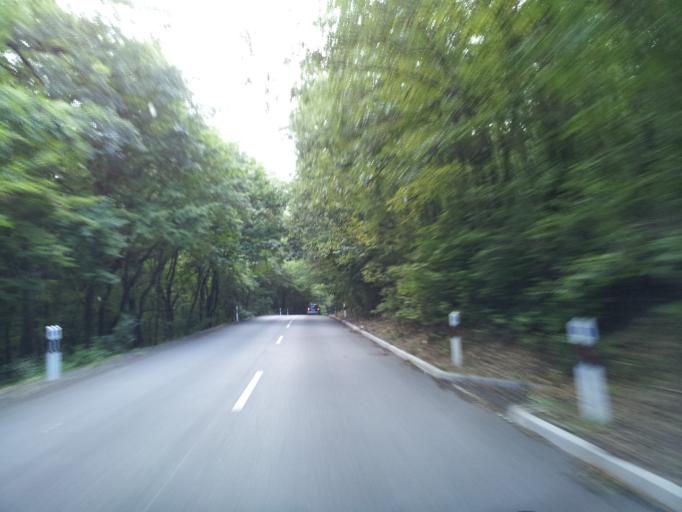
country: HU
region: Pest
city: Nagymaros
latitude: 47.8348
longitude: 18.9609
